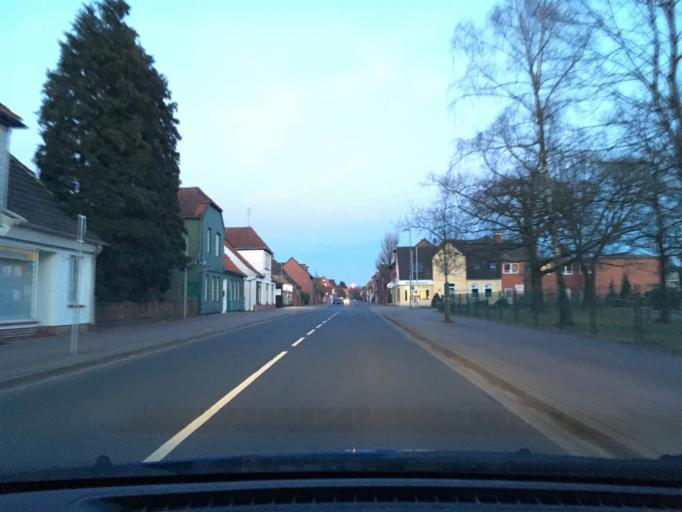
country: DE
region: Lower Saxony
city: Rotenburg
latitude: 53.1101
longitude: 9.4100
